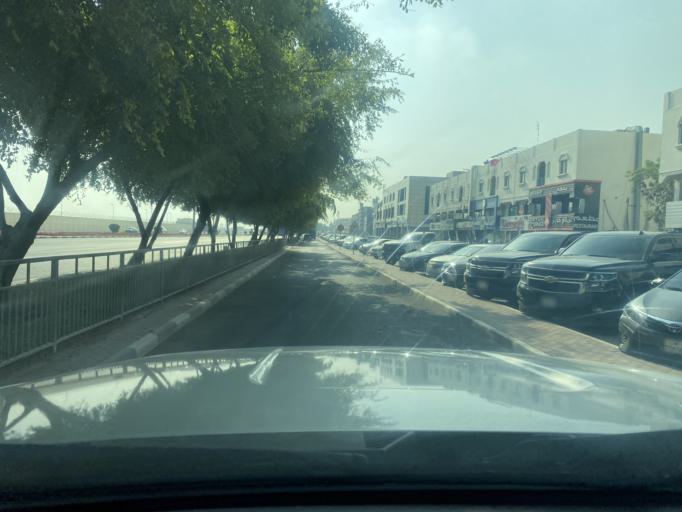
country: QA
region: Baladiyat ad Dawhah
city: Doha
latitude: 25.2435
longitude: 51.5692
